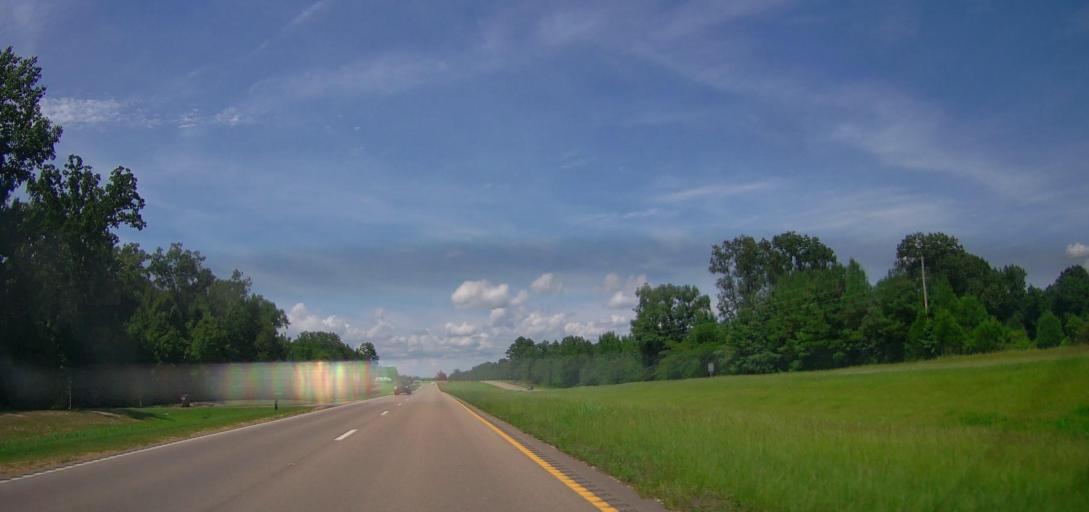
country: US
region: Mississippi
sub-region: Lee County
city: Nettleton
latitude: 33.9671
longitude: -88.6139
